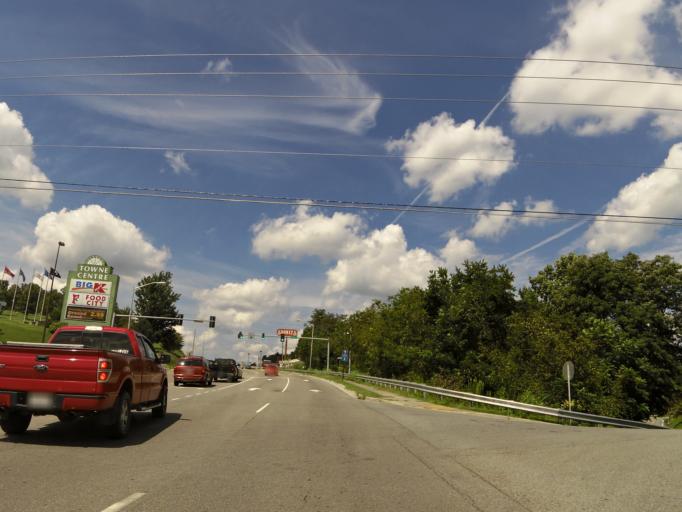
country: US
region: Virginia
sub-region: Washington County
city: Abingdon
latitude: 36.7023
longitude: -81.9741
